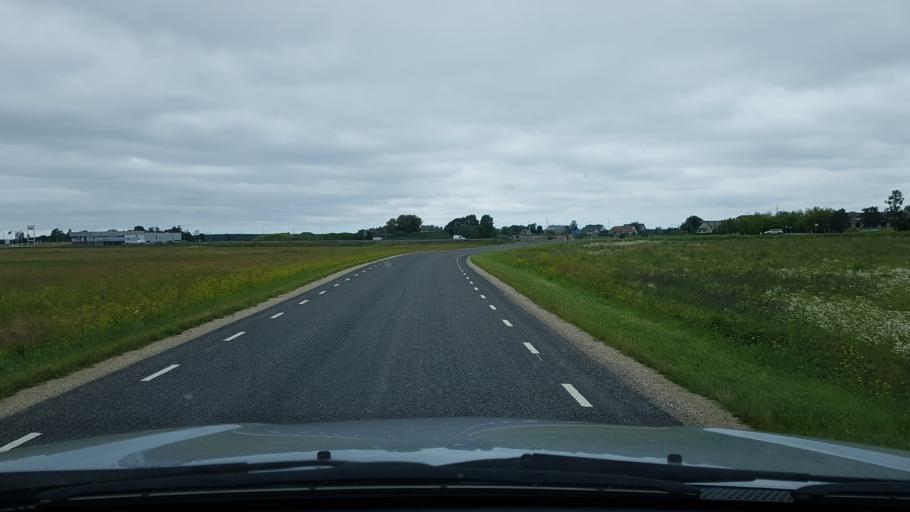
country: EE
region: Ida-Virumaa
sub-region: Narva linn
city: Narva
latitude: 59.3868
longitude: 28.1311
